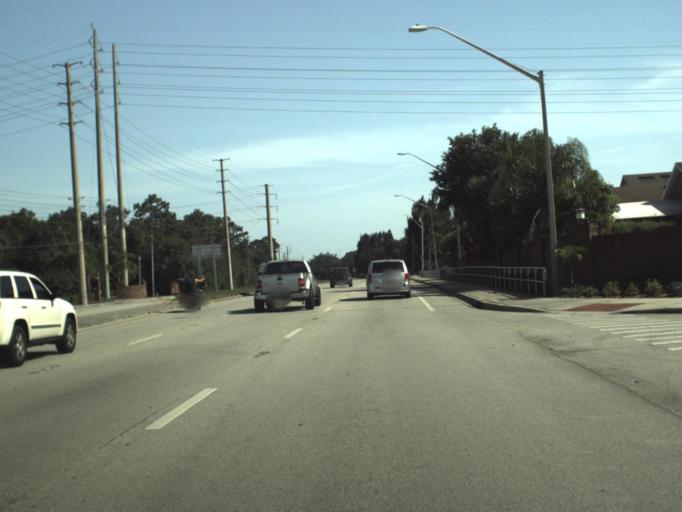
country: US
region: Florida
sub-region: Seminole County
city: Oviedo
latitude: 28.6398
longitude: -81.2082
